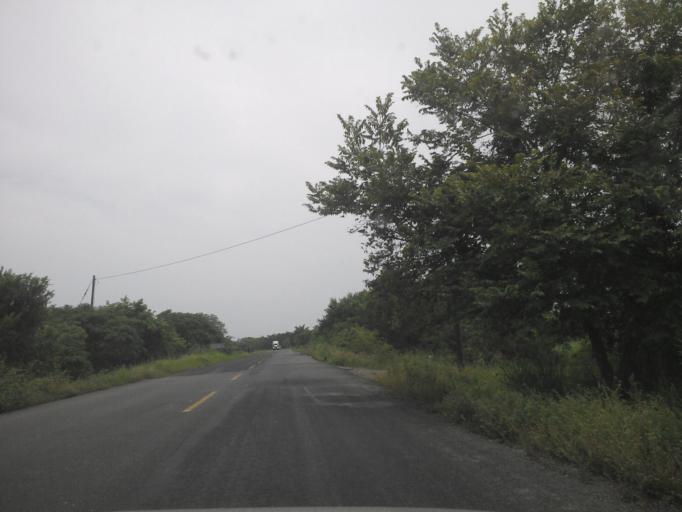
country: MX
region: Veracruz
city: Nautla
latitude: 20.2221
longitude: -96.8123
